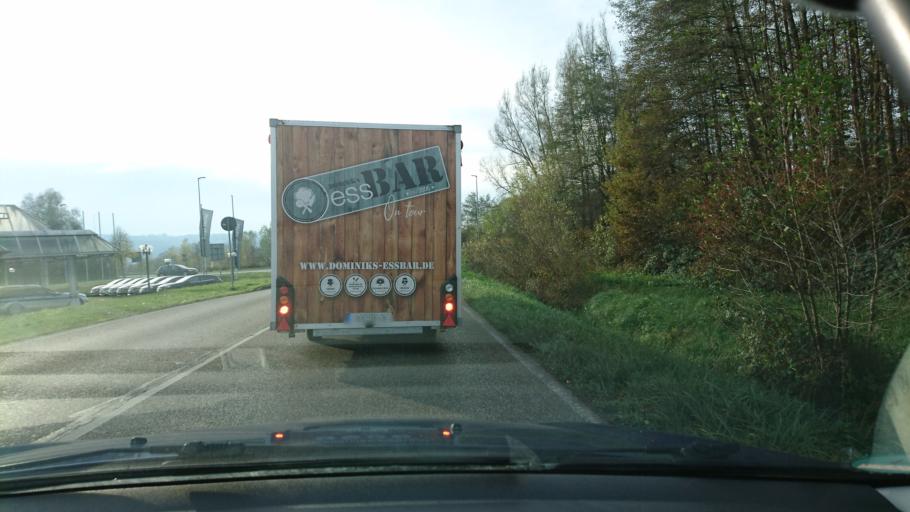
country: DE
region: Baden-Wuerttemberg
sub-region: Regierungsbezirk Stuttgart
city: Schorndorf
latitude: 48.8069
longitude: 9.5080
